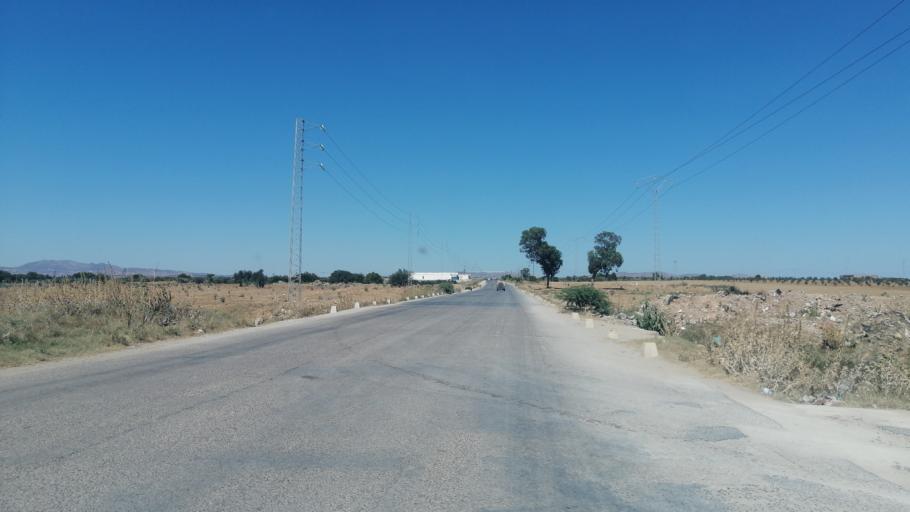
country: TN
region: Al Qayrawan
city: Sbikha
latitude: 36.1275
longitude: 10.1001
